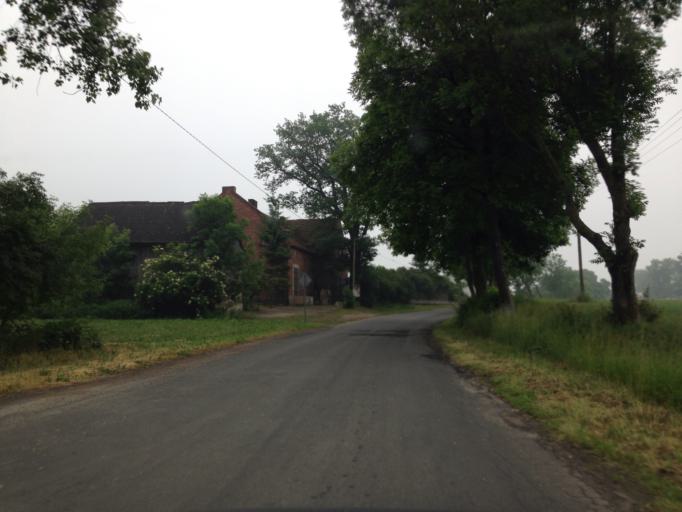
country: PL
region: Kujawsko-Pomorskie
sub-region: Powiat brodnicki
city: Jablonowo Pomorskie
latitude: 53.3994
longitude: 19.2243
